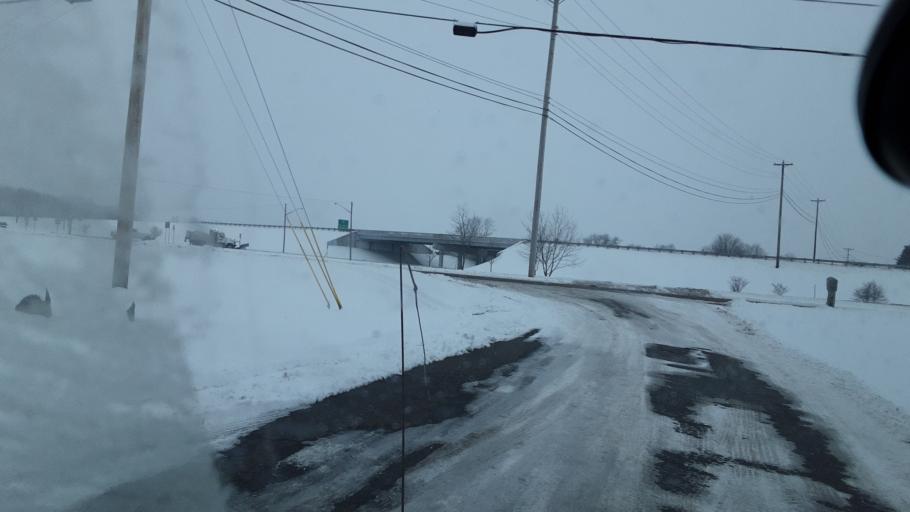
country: US
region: Ohio
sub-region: Licking County
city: Hebron
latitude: 39.9628
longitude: -82.4792
